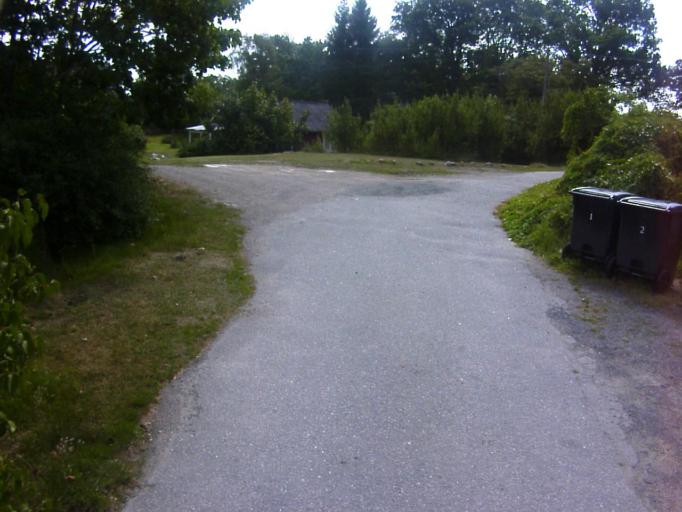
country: SE
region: Blekinge
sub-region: Karlshamns Kommun
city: Morrum
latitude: 56.1586
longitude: 14.6789
